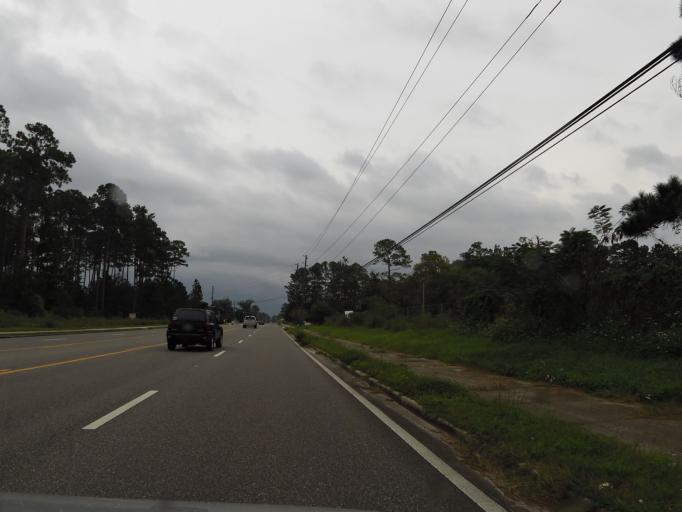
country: US
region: Florida
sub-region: Clay County
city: Lakeside
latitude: 30.1145
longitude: -81.8207
